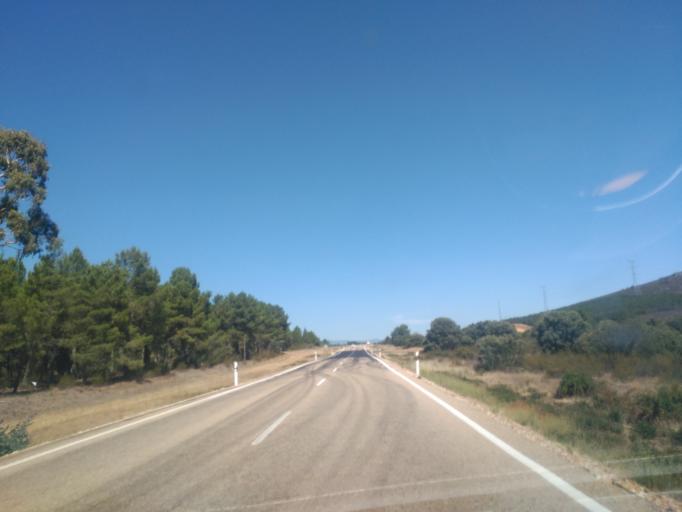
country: ES
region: Castille and Leon
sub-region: Provincia de Zamora
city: Tabara
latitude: 41.8708
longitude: -6.0073
